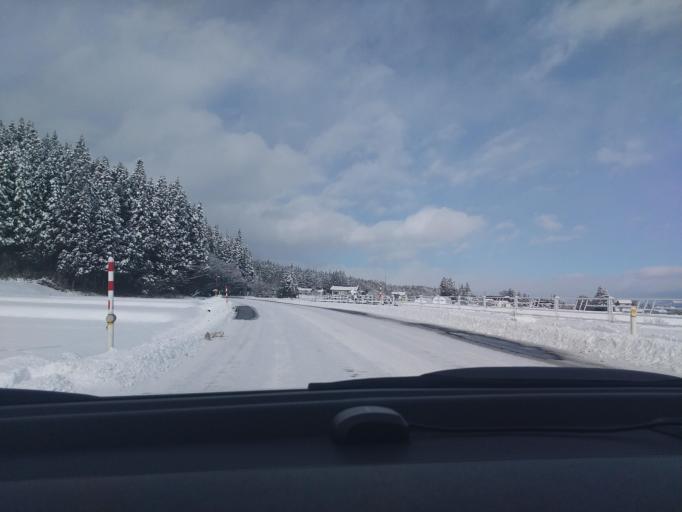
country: JP
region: Iwate
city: Hanamaki
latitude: 39.4821
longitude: 141.1043
